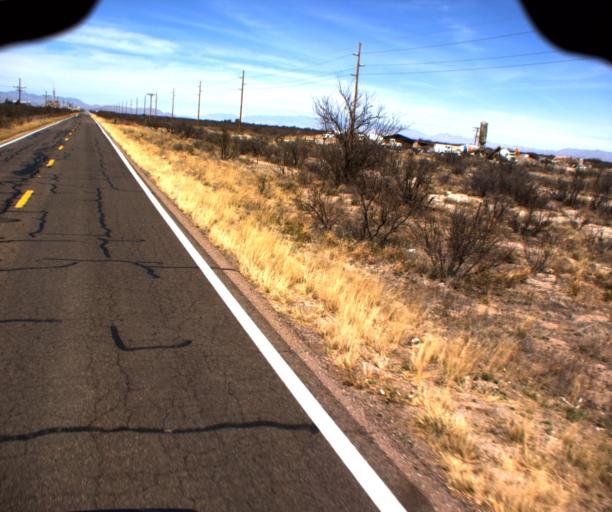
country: US
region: Arizona
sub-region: Cochise County
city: Willcox
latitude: 32.0238
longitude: -109.8728
